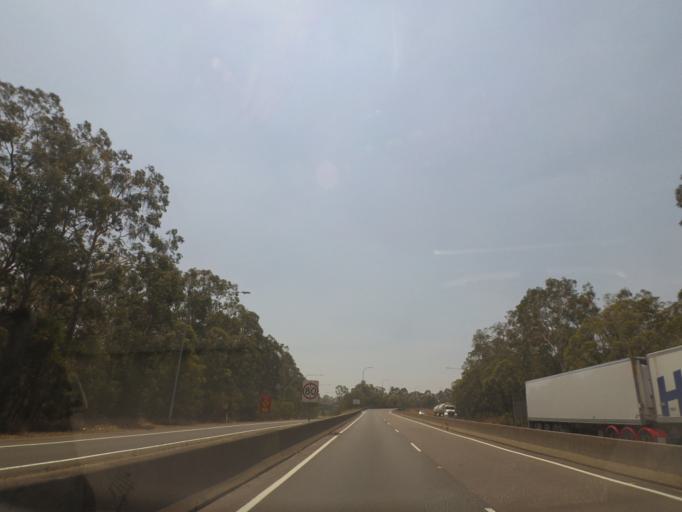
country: AU
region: New South Wales
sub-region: Newcastle
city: Beresfield
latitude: -32.8103
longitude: 151.6450
